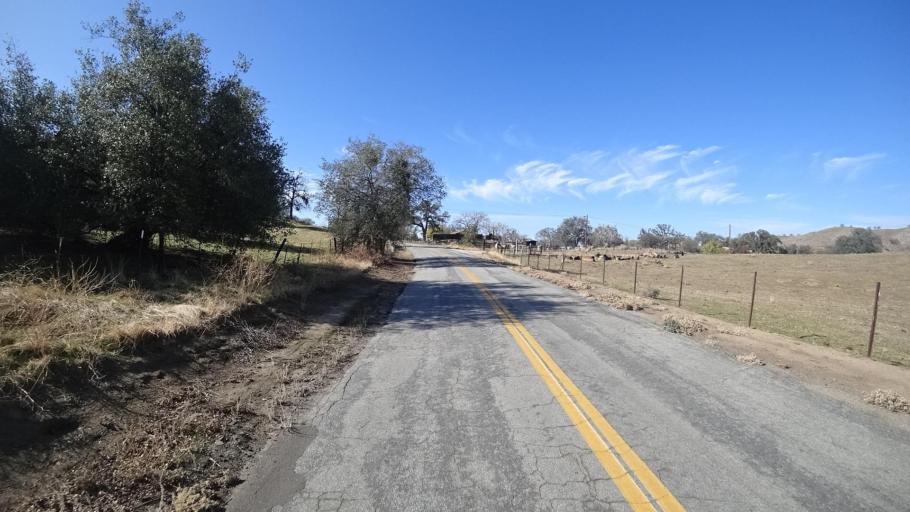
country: US
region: California
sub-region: Tulare County
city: Richgrove
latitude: 35.6997
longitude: -118.8416
